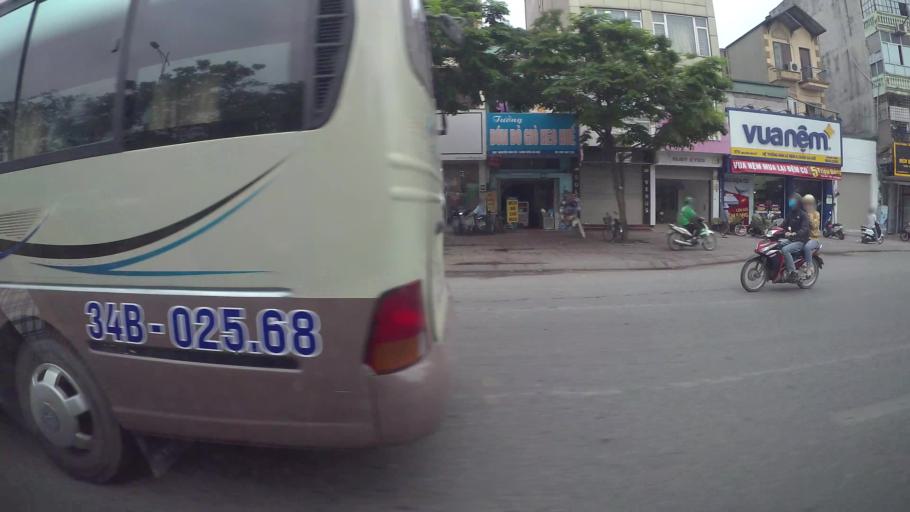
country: VN
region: Ha Noi
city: Hoan Kiem
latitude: 21.0512
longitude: 105.8851
